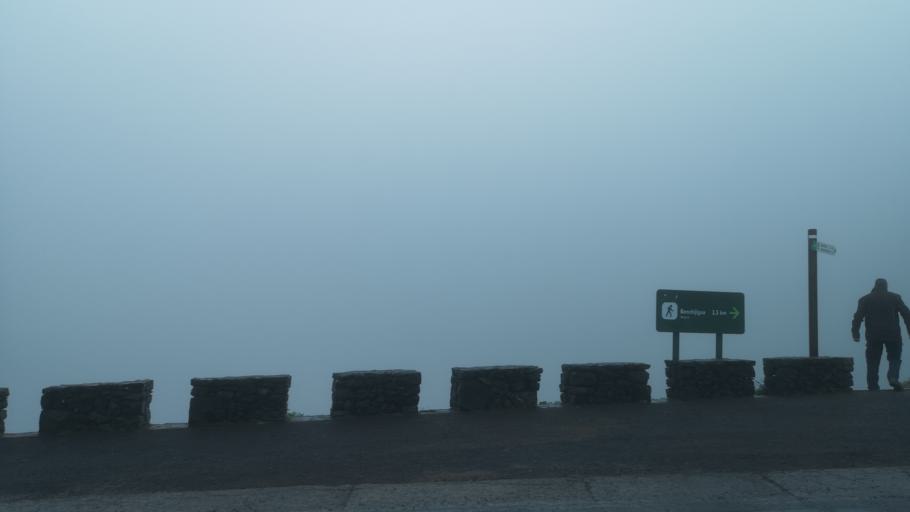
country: ES
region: Canary Islands
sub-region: Provincia de Santa Cruz de Tenerife
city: Alajero
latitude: 28.1073
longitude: -17.2135
